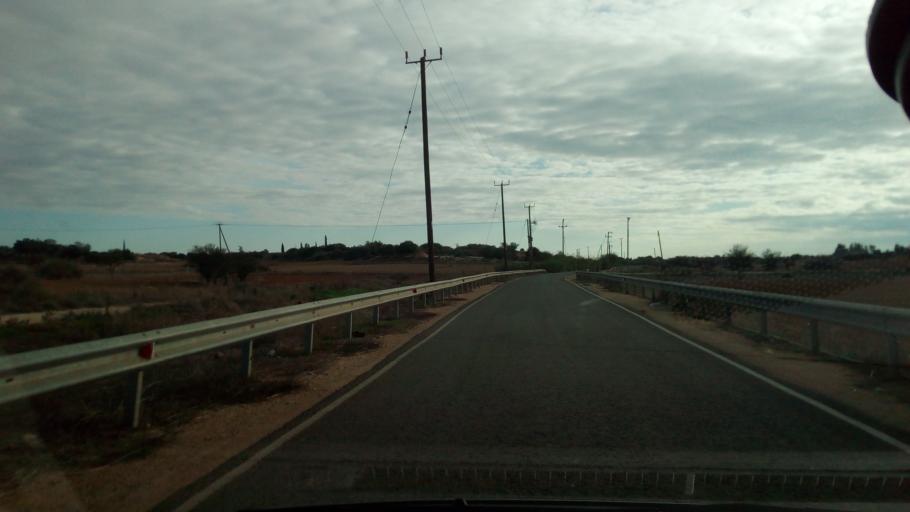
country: CY
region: Ammochostos
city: Frenaros
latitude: 35.0490
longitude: 33.8875
